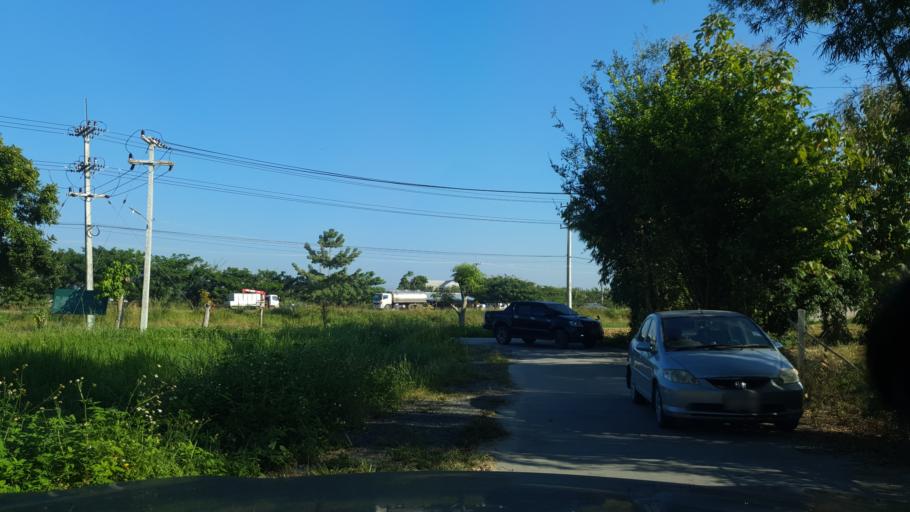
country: TH
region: Chiang Mai
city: San Kamphaeng
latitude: 18.7161
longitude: 99.1468
